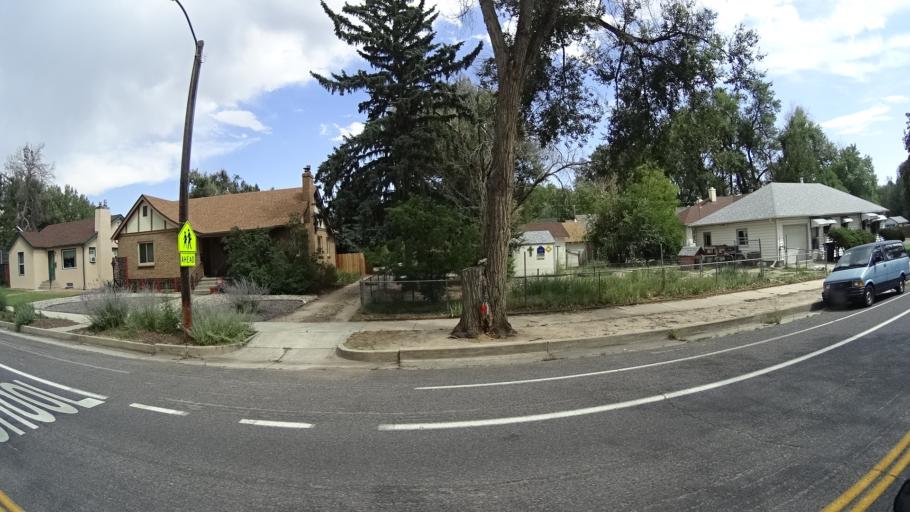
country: US
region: Colorado
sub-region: El Paso County
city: Colorado Springs
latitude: 38.8452
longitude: -104.8078
